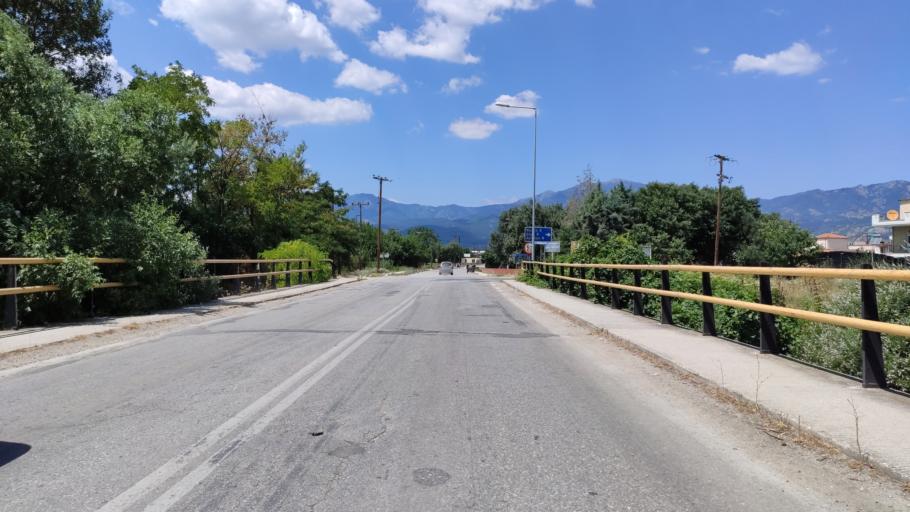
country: GR
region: East Macedonia and Thrace
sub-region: Nomos Rodopis
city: Komotini
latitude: 41.1274
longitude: 25.3850
